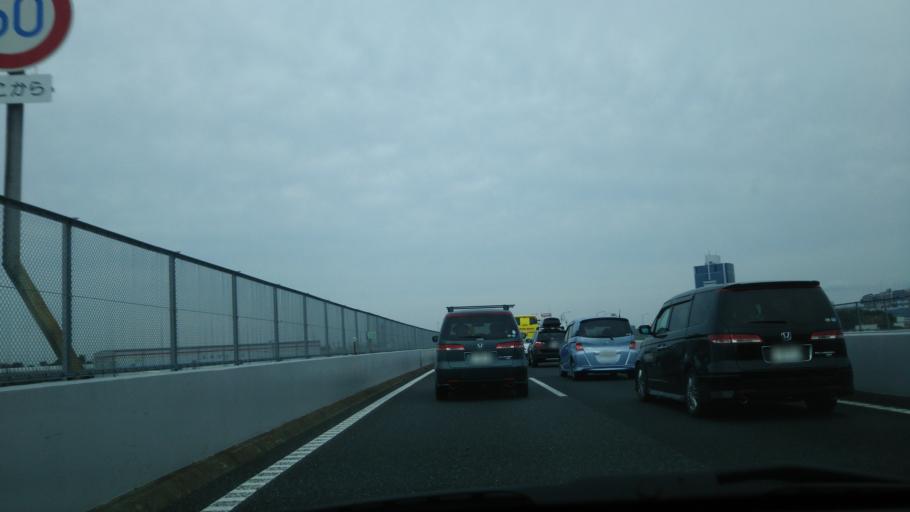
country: JP
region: Kanagawa
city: Atsugi
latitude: 35.4168
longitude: 139.3507
